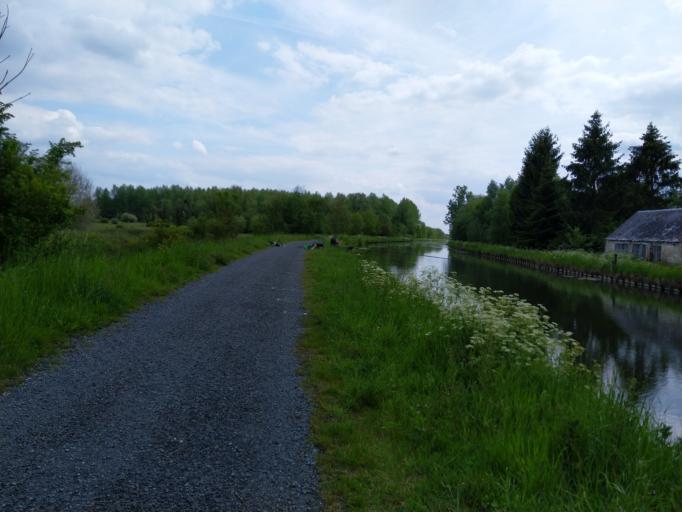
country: FR
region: Nord-Pas-de-Calais
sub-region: Departement du Nord
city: Landrecies
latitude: 50.0754
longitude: 3.6470
